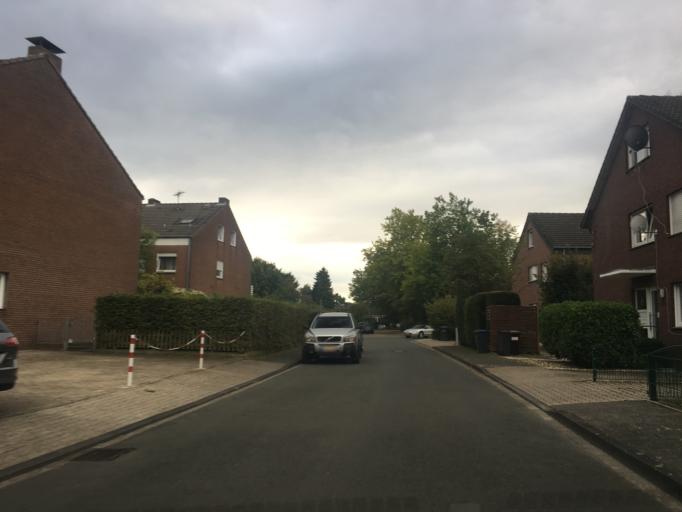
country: DE
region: North Rhine-Westphalia
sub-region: Regierungsbezirk Munster
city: Muenster
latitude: 51.9534
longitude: 7.5437
